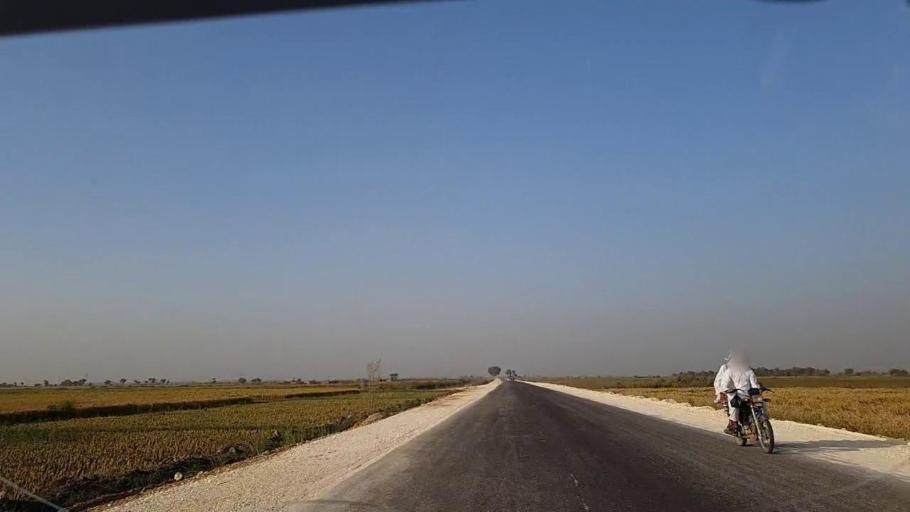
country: PK
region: Sindh
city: Rustam jo Goth
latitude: 27.9827
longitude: 68.8065
